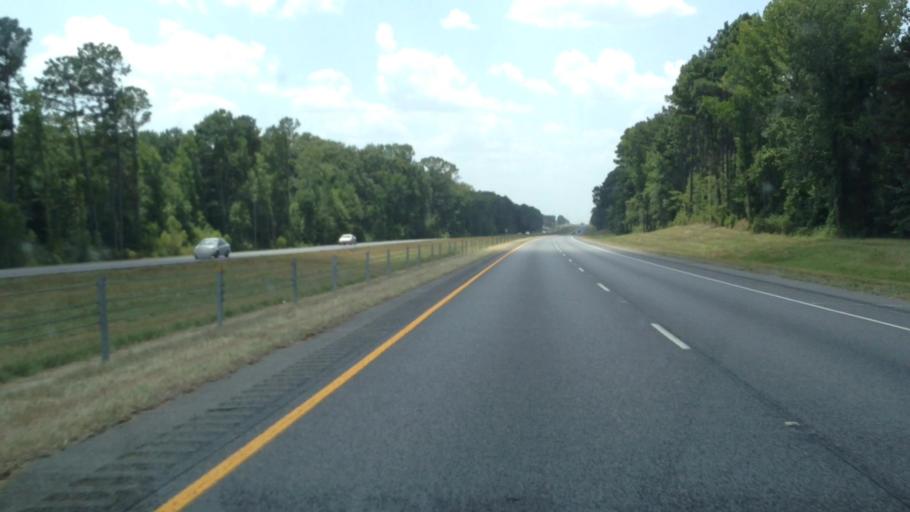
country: US
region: Louisiana
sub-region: Lincoln Parish
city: Ruston
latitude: 32.5298
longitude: -92.4554
